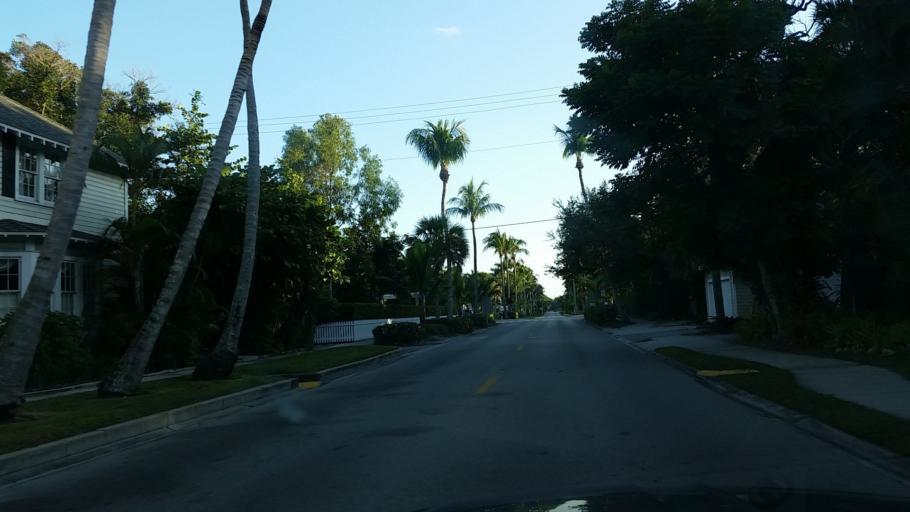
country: US
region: Florida
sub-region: Collier County
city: Naples
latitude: 26.1327
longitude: -81.8048
